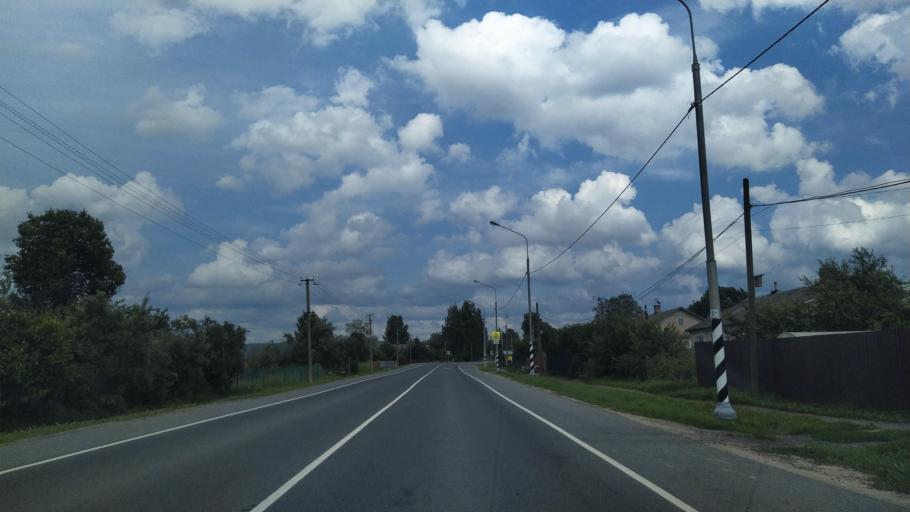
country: RU
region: Pskov
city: Dno
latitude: 58.0610
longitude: 29.9830
